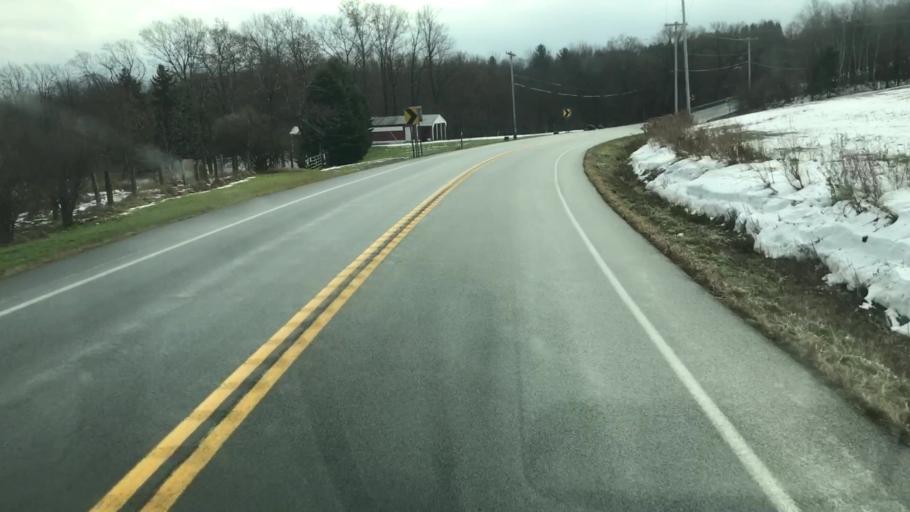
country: US
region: New York
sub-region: Cayuga County
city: Moravia
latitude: 42.8307
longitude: -76.3519
